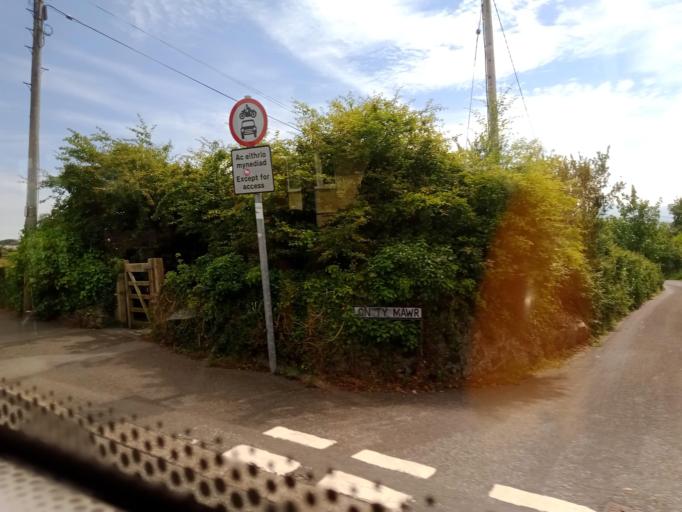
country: GB
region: Wales
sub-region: Gwynedd
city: Bangor
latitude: 53.2415
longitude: -4.1482
